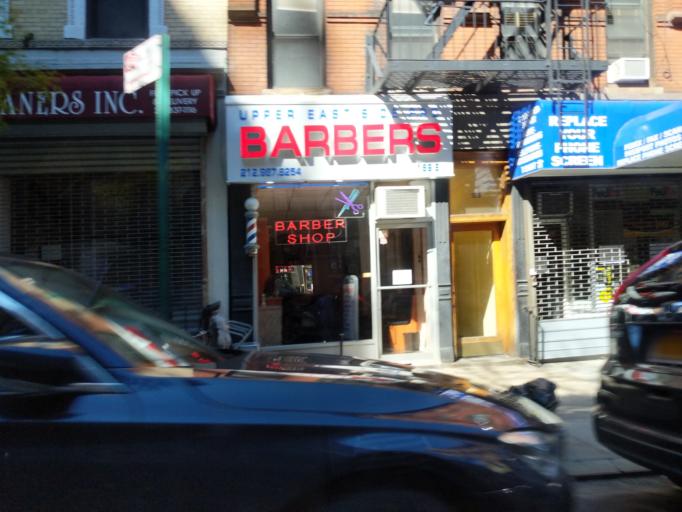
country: US
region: New York
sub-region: New York County
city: Manhattan
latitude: 40.7829
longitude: -73.9519
